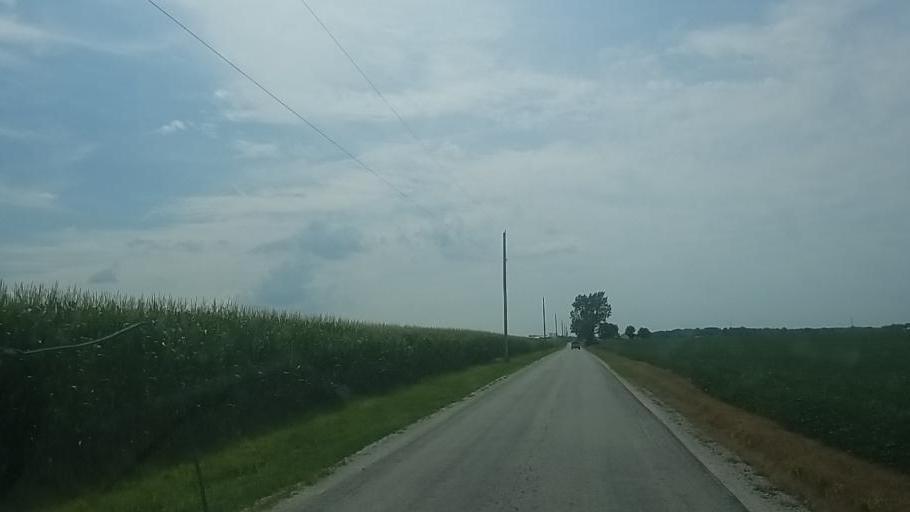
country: US
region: Ohio
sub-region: Hardin County
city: Forest
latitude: 40.7600
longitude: -83.5421
